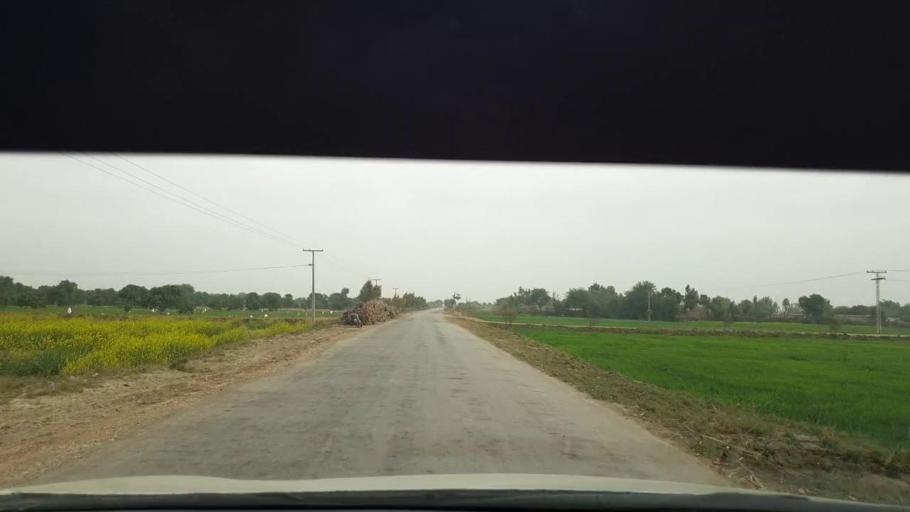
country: PK
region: Sindh
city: Berani
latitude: 25.7769
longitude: 68.8902
